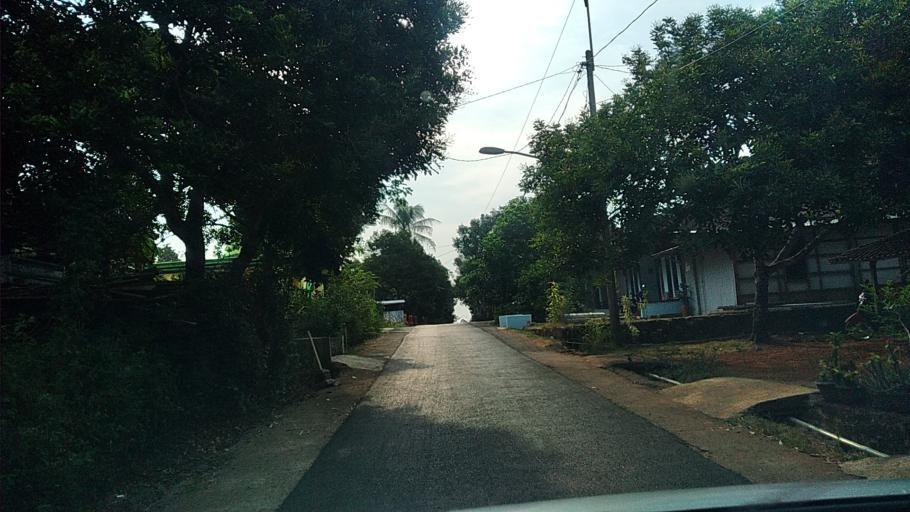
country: ID
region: Central Java
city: Ungaran
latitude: -7.0856
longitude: 110.3938
